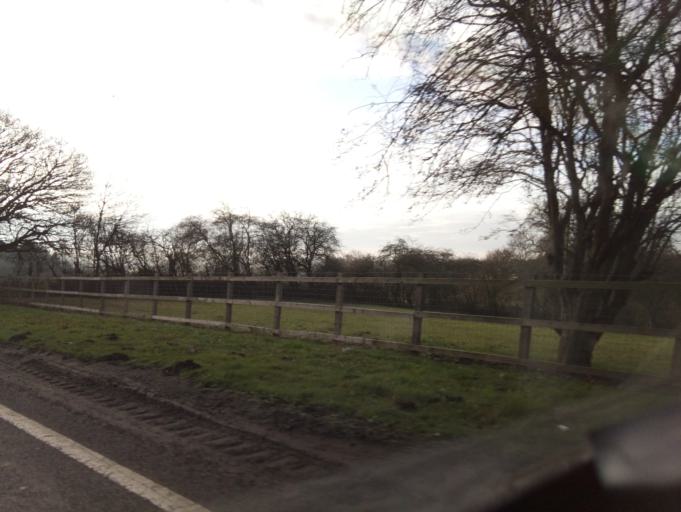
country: GB
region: England
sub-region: Warwickshire
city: Curdworth
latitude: 52.5739
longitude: -1.7670
